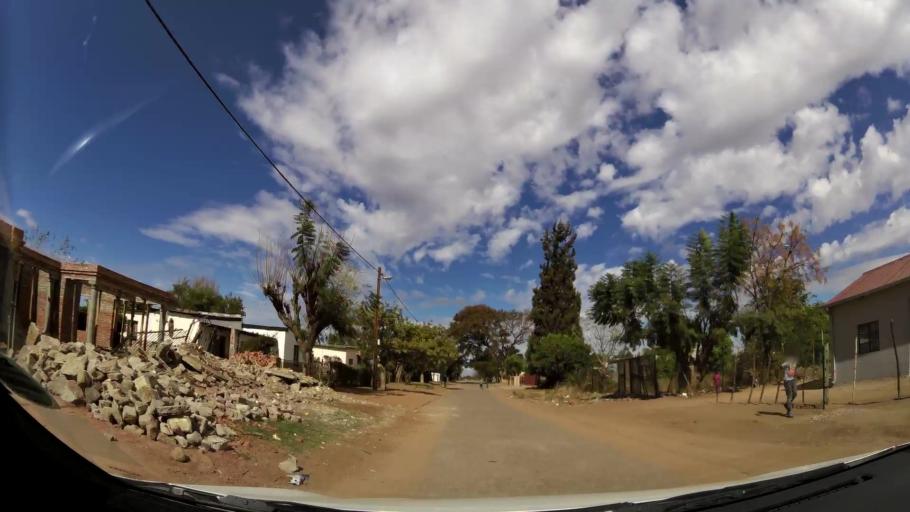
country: ZA
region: Limpopo
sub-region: Waterberg District Municipality
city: Bela-Bela
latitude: -24.8873
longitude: 28.3146
